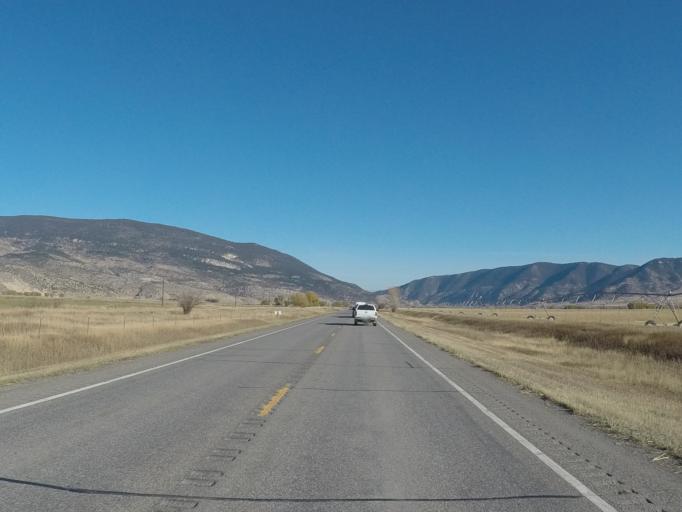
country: US
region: Montana
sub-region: Park County
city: Livingston
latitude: 45.5370
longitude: -110.6028
